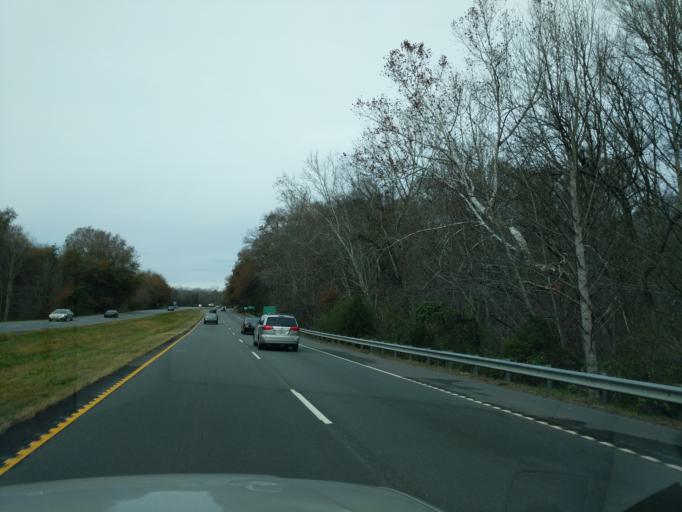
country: US
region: South Carolina
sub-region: Anderson County
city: Pendleton
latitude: 34.6444
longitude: -82.7990
